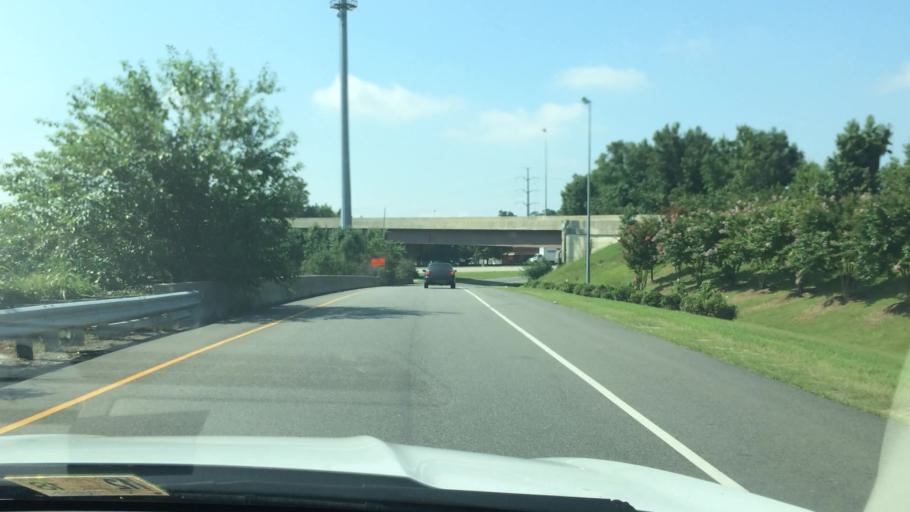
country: US
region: Virginia
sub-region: City of Hampton
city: Hampton
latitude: 37.0412
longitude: -76.3978
